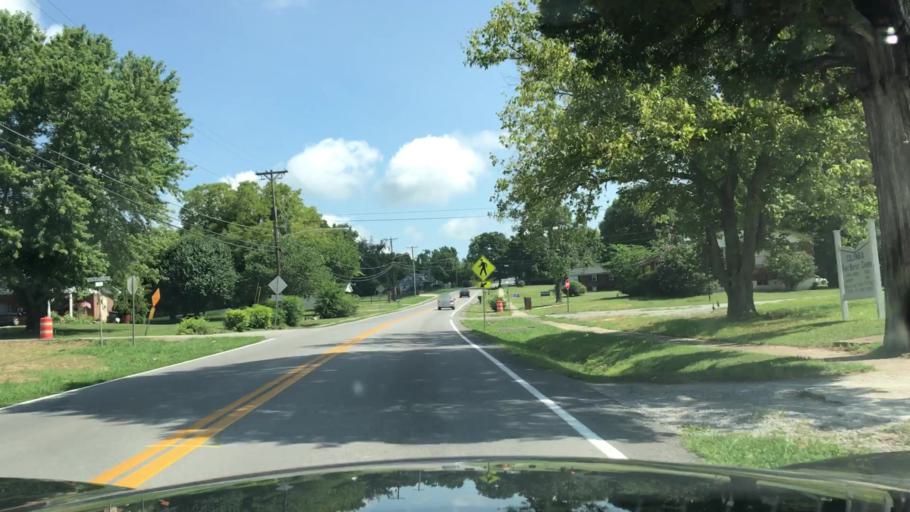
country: US
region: Kentucky
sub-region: Adair County
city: Columbia
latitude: 37.0934
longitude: -85.3168
